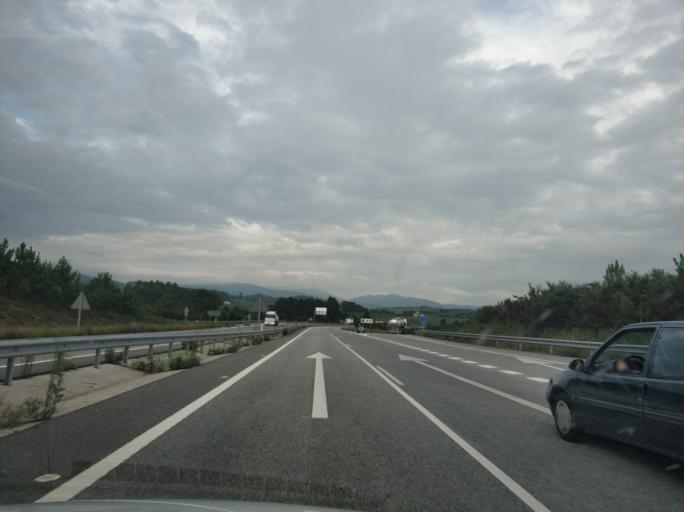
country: ES
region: Asturias
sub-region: Province of Asturias
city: Navia
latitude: 43.5349
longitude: -6.6530
